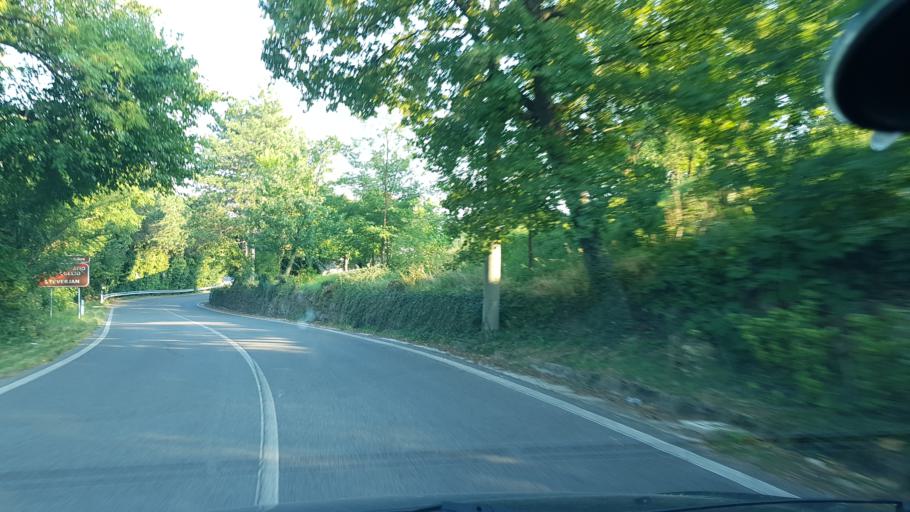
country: IT
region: Friuli Venezia Giulia
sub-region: Provincia di Gorizia
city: San Floriano del Collio
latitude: 45.9838
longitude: 13.5994
